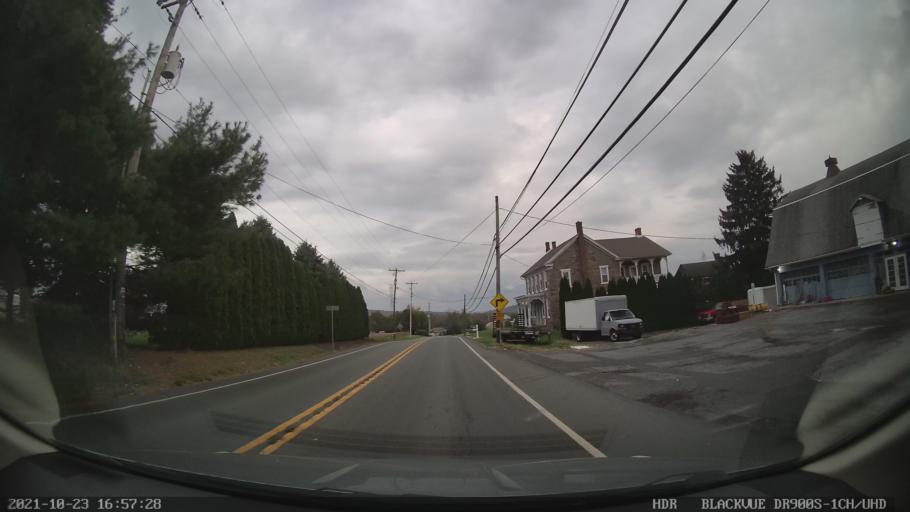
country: US
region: Pennsylvania
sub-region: Berks County
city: Bally
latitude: 40.4464
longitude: -75.5496
